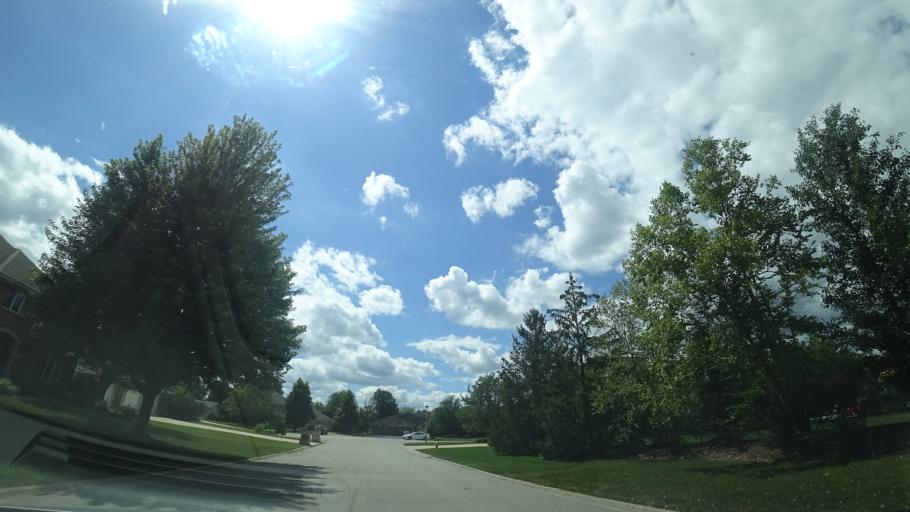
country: US
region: Illinois
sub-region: Will County
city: Homer Glen
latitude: 41.5792
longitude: -87.9131
